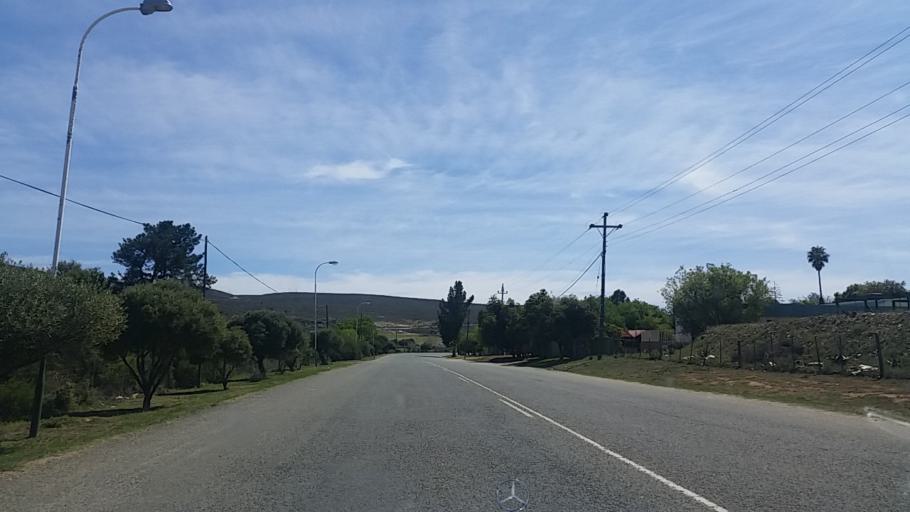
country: ZA
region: Western Cape
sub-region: Eden District Municipality
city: Knysna
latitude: -33.6514
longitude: 23.1347
